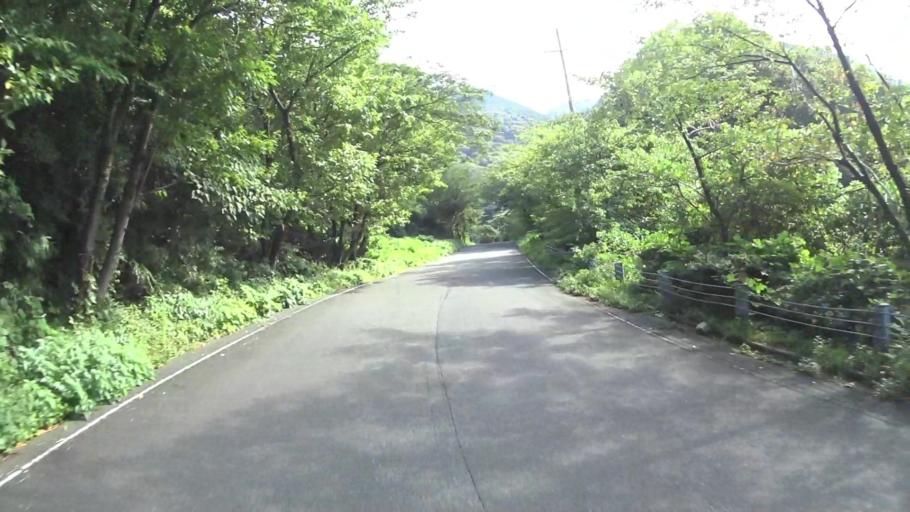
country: JP
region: Kyoto
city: Miyazu
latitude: 35.7738
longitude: 135.2246
